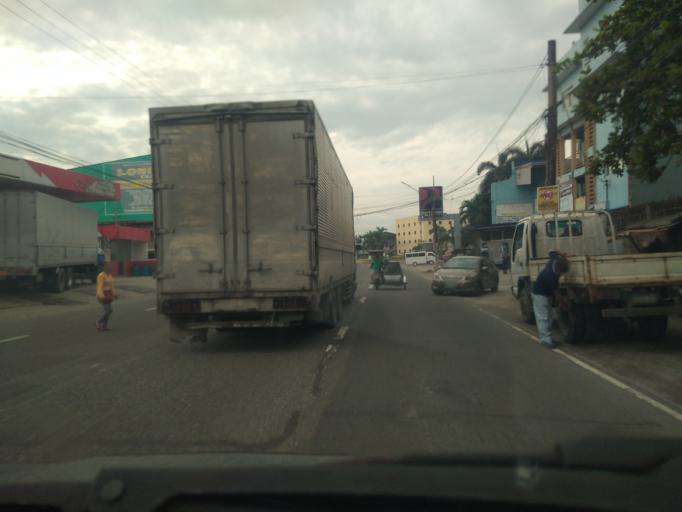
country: PH
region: Central Luzon
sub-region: Province of Pampanga
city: San Fernando
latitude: 15.0238
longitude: 120.6979
